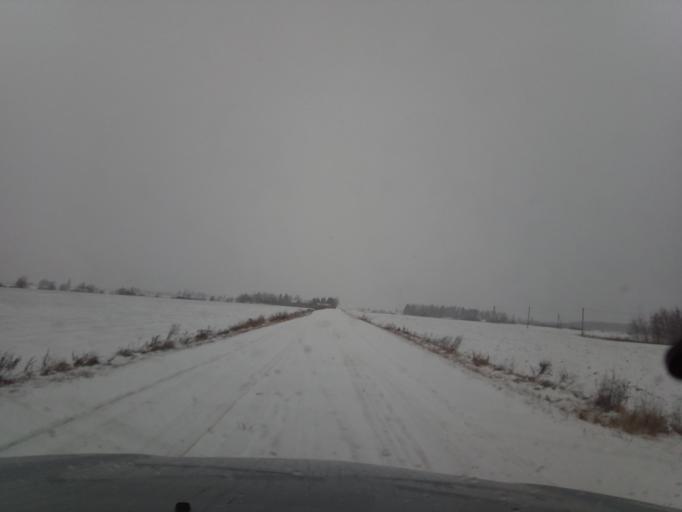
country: LT
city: Ramygala
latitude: 55.5612
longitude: 24.3590
